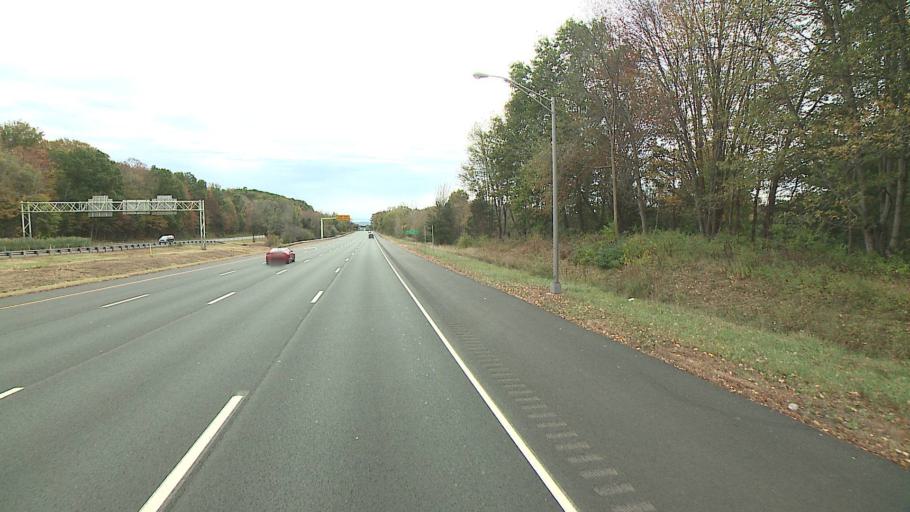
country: US
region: Connecticut
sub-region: Middlesex County
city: Cromwell
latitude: 41.6178
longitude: -72.6821
